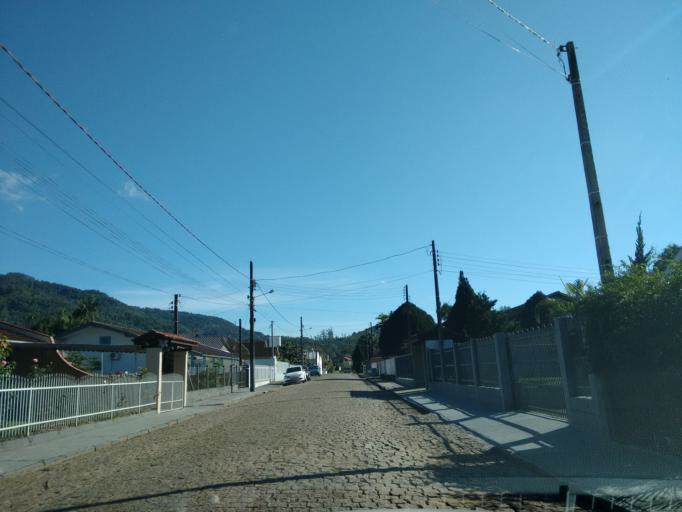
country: BR
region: Santa Catarina
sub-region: Pomerode
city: Pomerode
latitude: -26.7280
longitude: -49.1716
